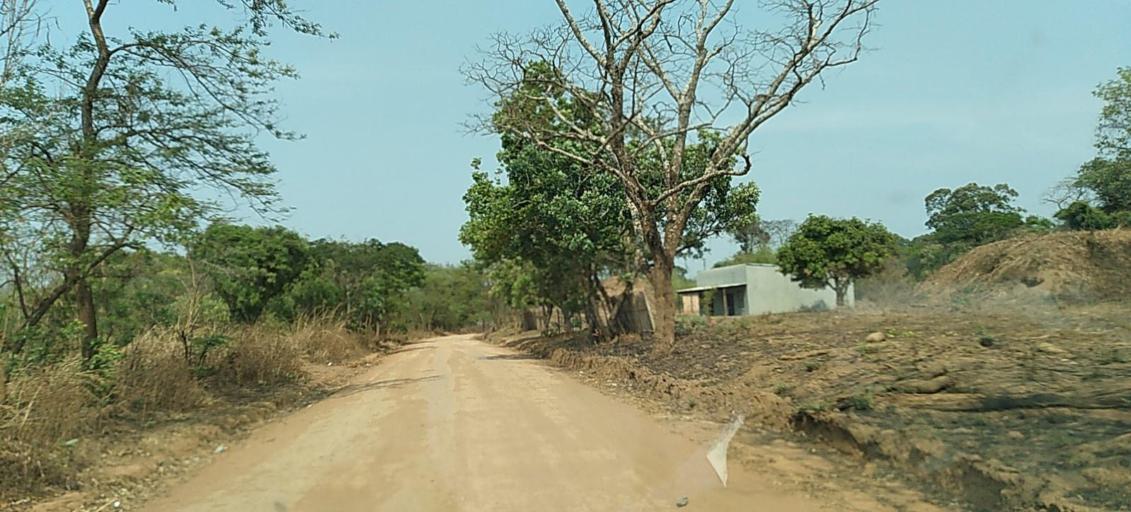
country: ZM
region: Copperbelt
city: Chililabombwe
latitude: -12.3397
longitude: 27.7155
